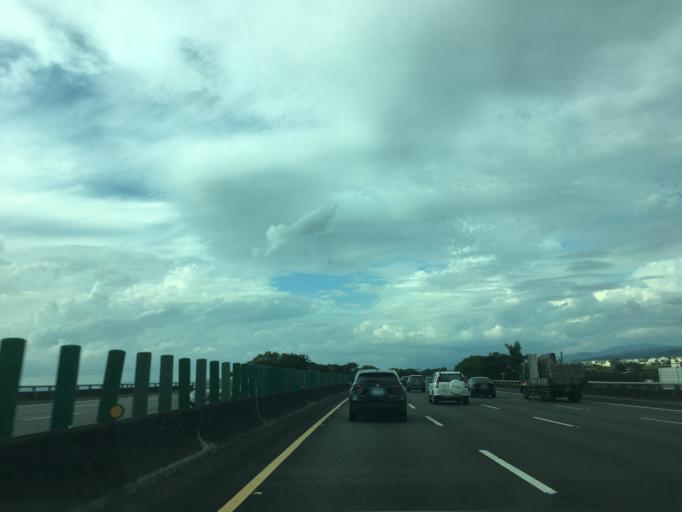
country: TW
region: Taiwan
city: Zhongxing New Village
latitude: 23.9715
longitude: 120.6487
